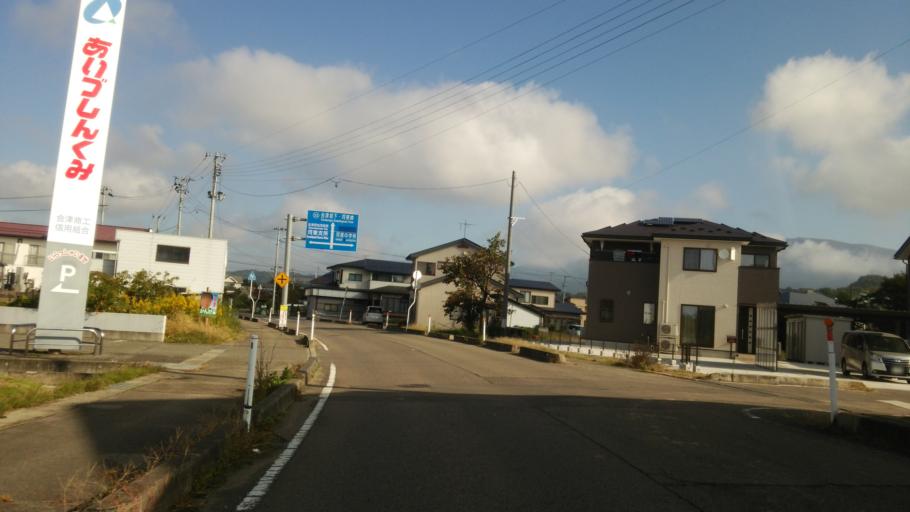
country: JP
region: Fukushima
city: Kitakata
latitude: 37.5507
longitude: 139.9342
